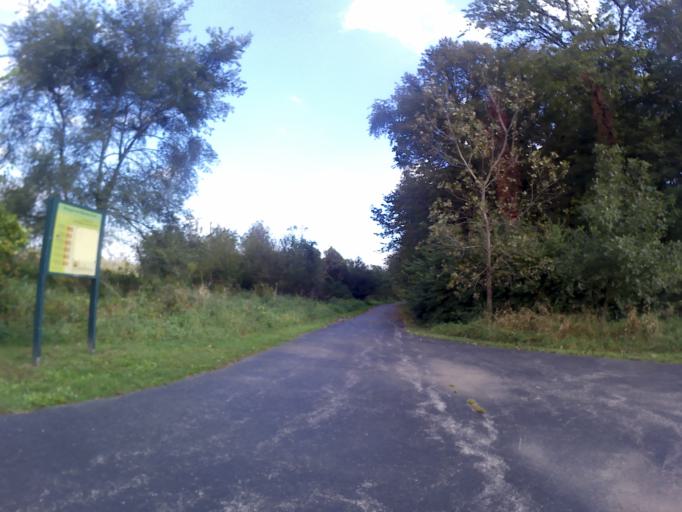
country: US
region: Illinois
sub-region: Will County
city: Bolingbrook
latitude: 41.7104
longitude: -88.0968
